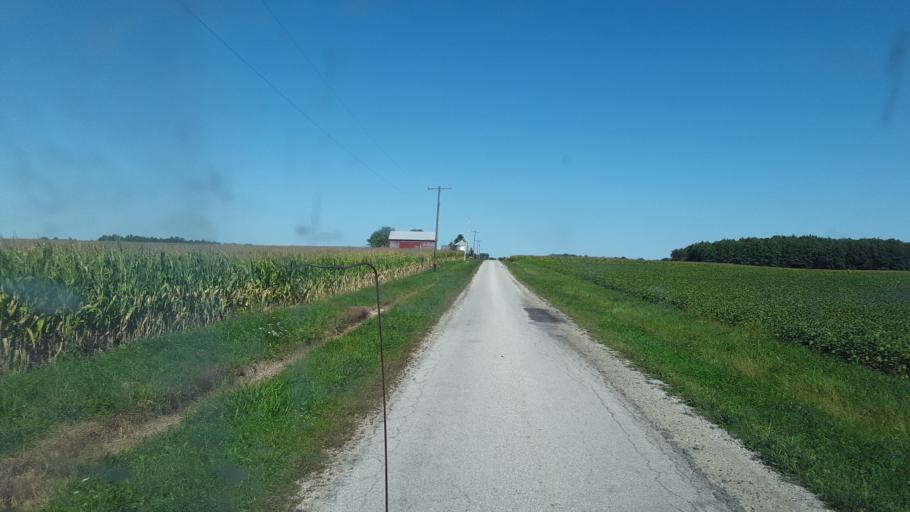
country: US
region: Ohio
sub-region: Sandusky County
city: Mount Carmel
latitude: 41.1629
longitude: -82.8997
